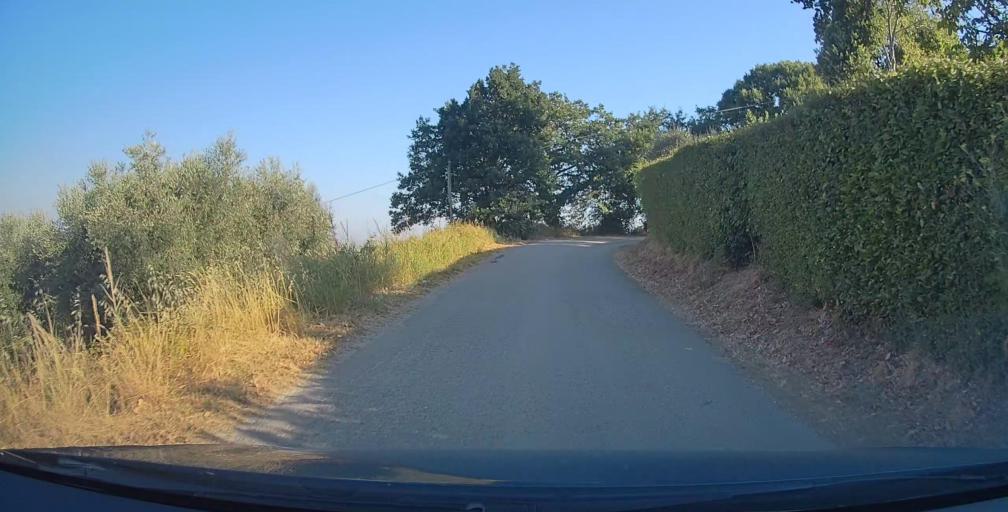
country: IT
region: Umbria
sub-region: Provincia di Terni
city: Calvi dell'Umbria
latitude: 42.3755
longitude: 12.5662
